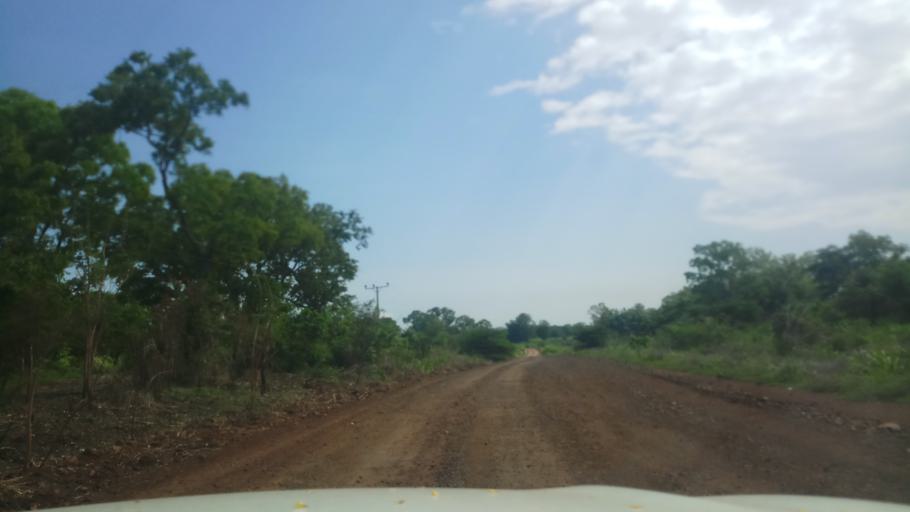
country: ET
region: Gambela
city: Gambela
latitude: 8.2052
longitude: 34.5117
